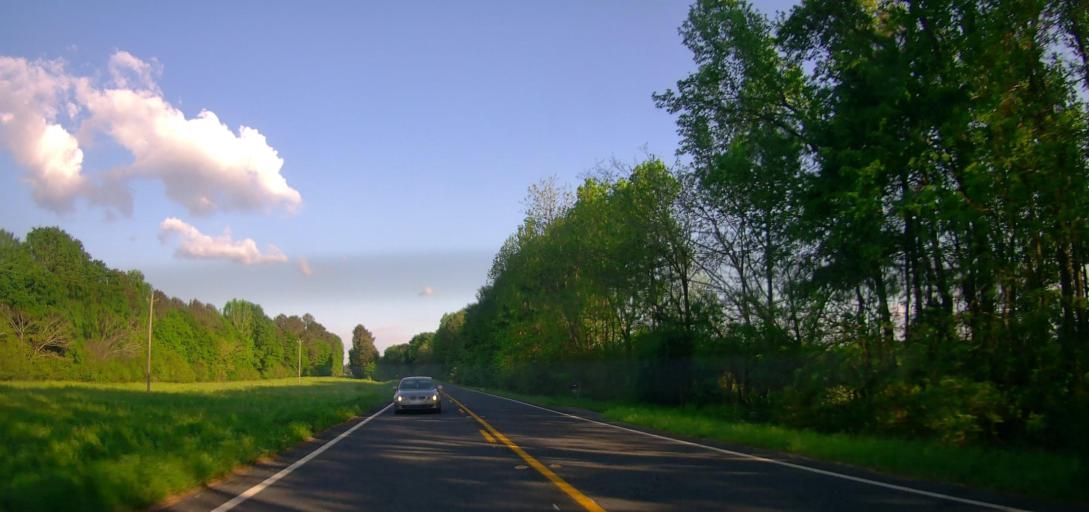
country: US
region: Georgia
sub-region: Jasper County
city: Monticello
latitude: 33.4107
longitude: -83.6044
